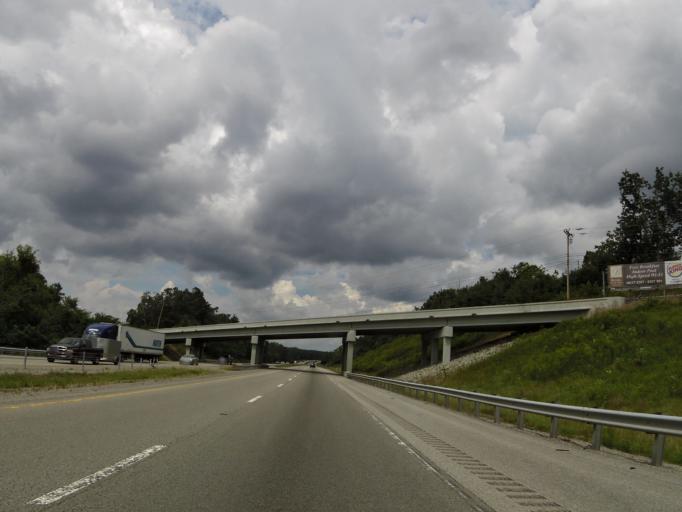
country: US
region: Tennessee
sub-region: Putnam County
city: Monterey
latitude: 36.1128
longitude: -85.2425
